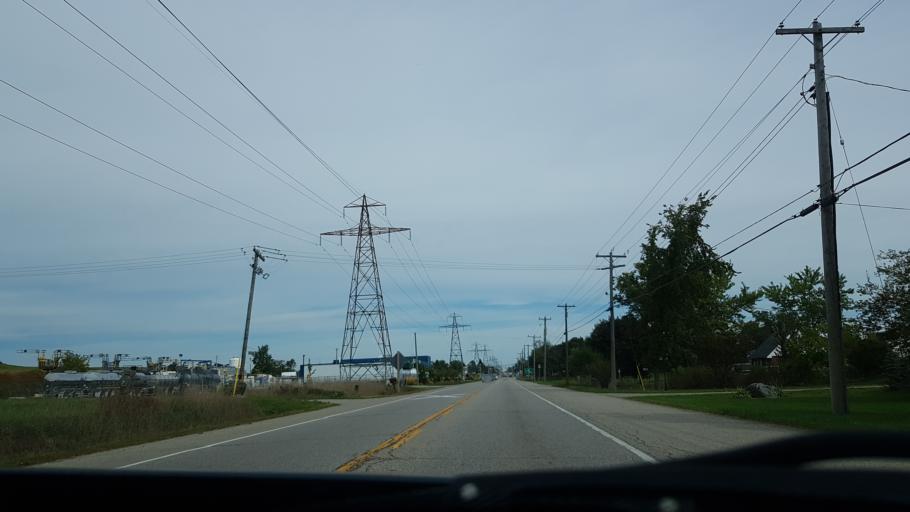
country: CA
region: Ontario
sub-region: Wellington County
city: Guelph
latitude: 43.4845
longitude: -80.2915
